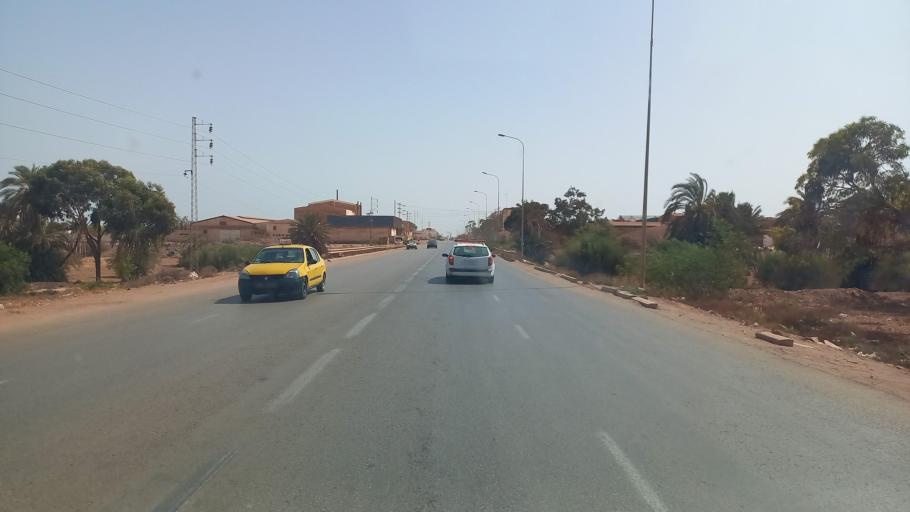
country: TN
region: Madanin
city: Medenine
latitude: 33.3440
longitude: 10.5116
